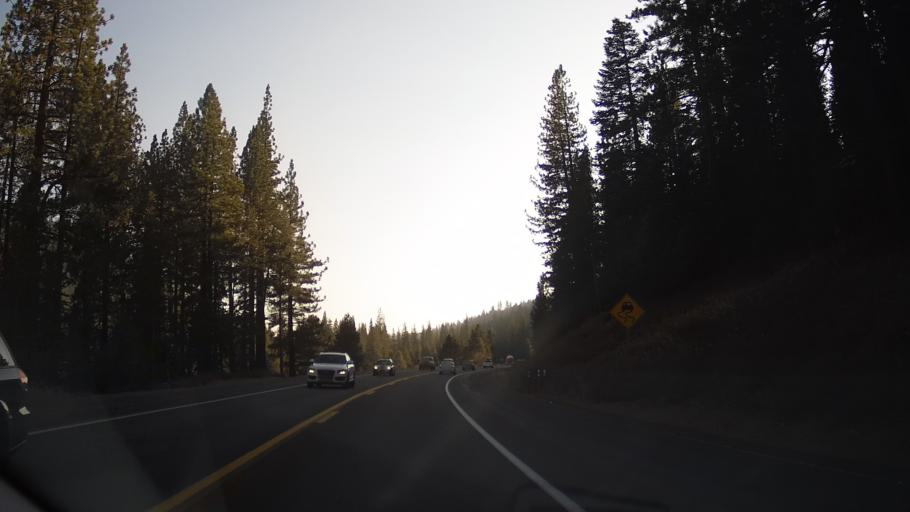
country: US
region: California
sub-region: Nevada County
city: Truckee
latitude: 39.2637
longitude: -120.2105
